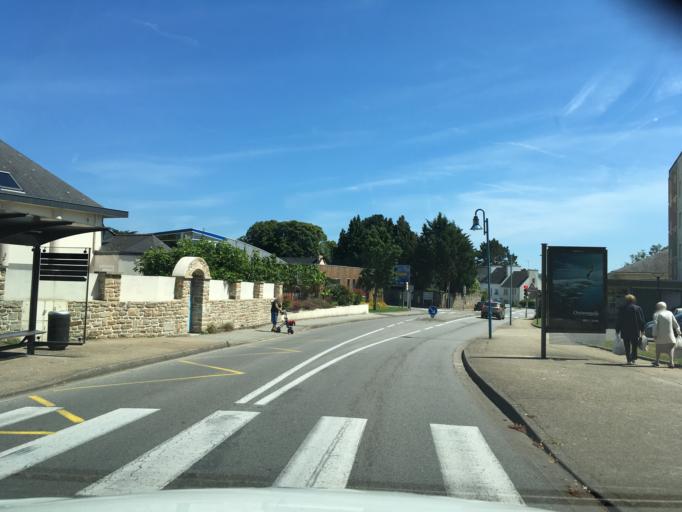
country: FR
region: Brittany
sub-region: Departement du Finistere
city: Quimper
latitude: 47.9888
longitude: -4.1305
